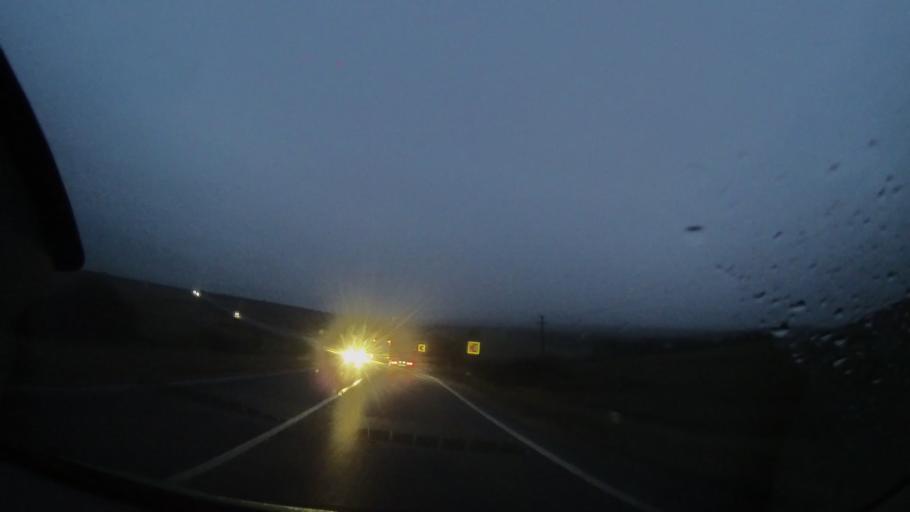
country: RO
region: Harghita
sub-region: Comuna Ditrau
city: Ditrau
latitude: 46.8267
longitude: 25.4916
